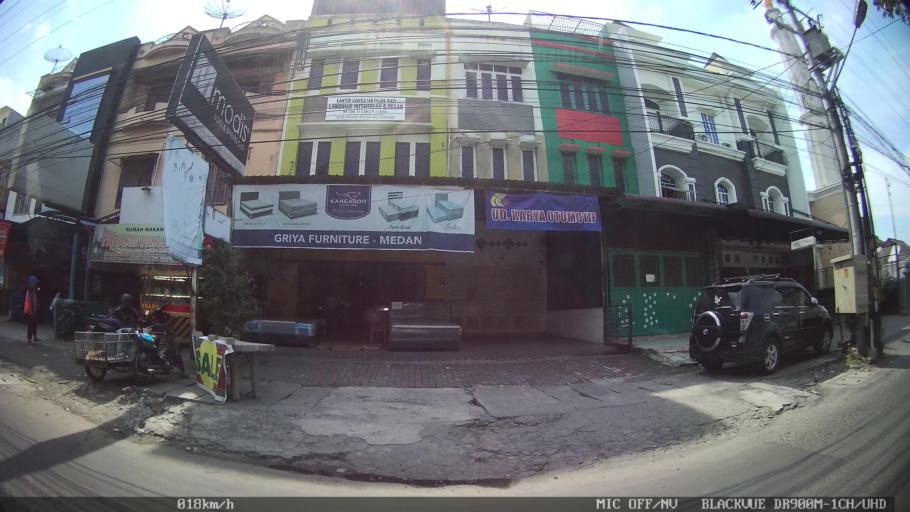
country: ID
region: North Sumatra
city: Medan
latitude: 3.6089
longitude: 98.6652
